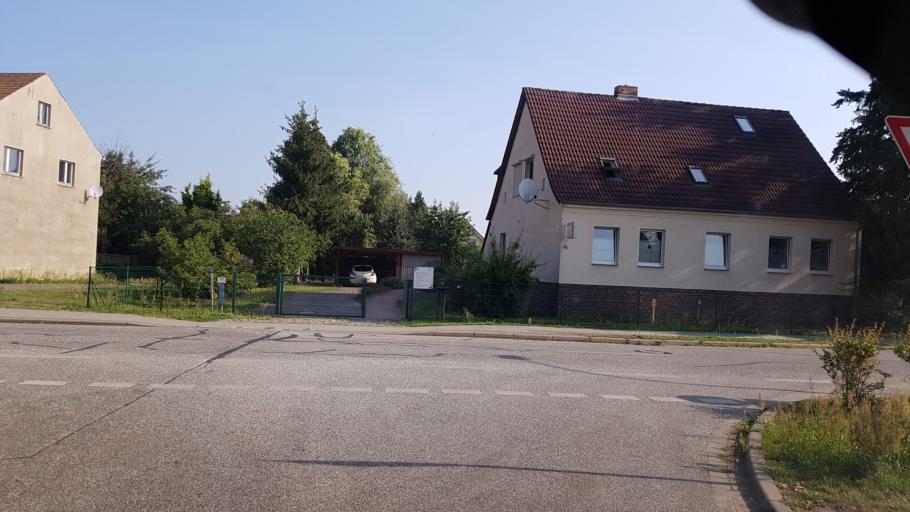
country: DE
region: Brandenburg
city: Drebkau
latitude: 51.6952
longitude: 14.2510
